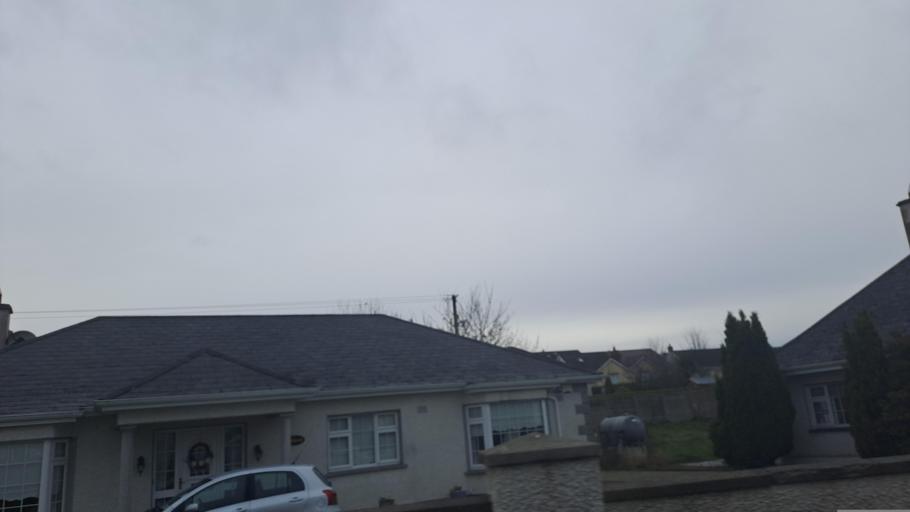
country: IE
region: Ulster
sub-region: An Cabhan
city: Virginia
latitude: 53.8379
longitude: -7.0794
